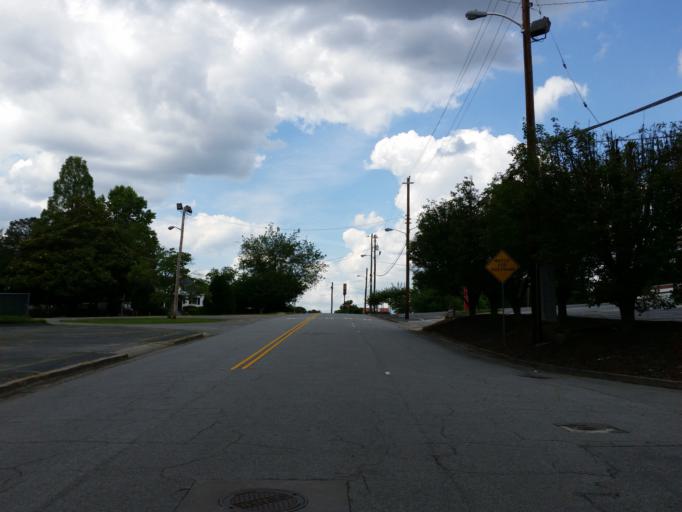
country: US
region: Georgia
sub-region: Cobb County
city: Marietta
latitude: 33.9490
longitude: -84.5304
